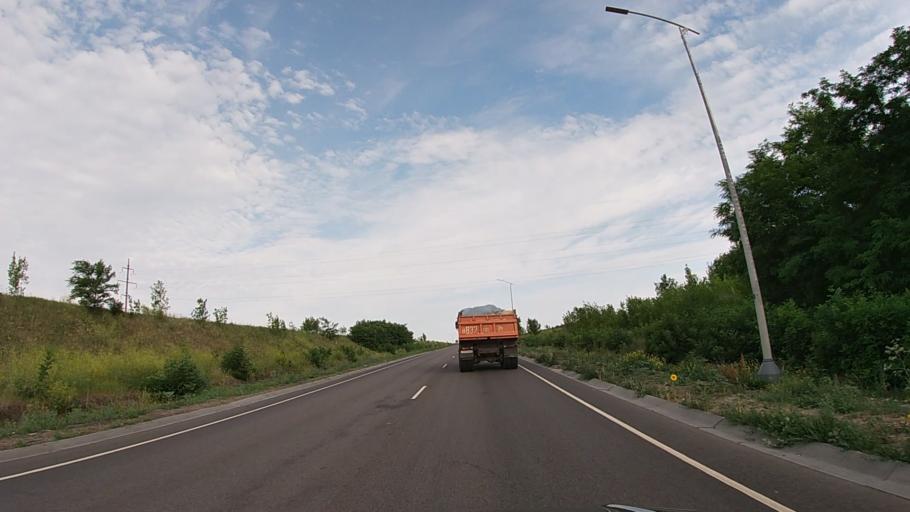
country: RU
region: Belgorod
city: Severnyy
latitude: 50.6700
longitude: 36.4860
